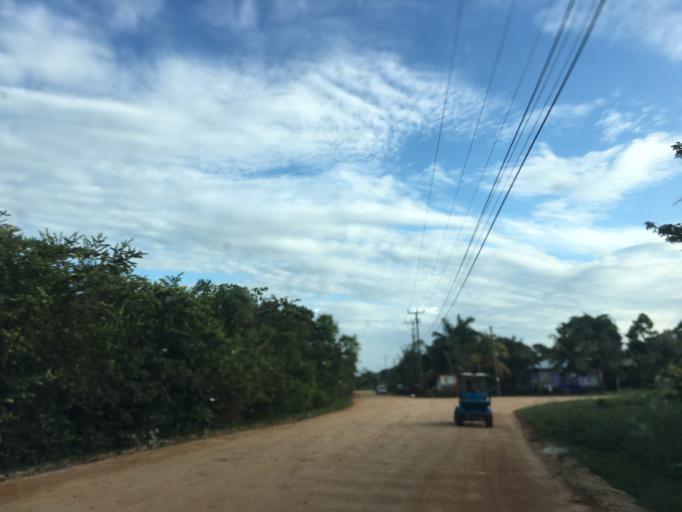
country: BZ
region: Stann Creek
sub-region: Dangriga
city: Dangriga
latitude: 16.8424
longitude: -88.2753
